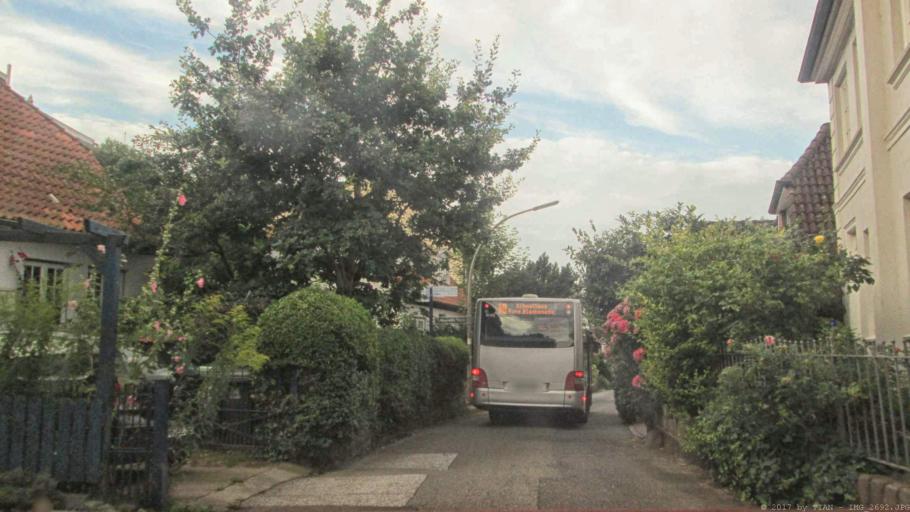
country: DE
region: Schleswig-Holstein
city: Halstenbek
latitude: 53.5591
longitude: 9.8037
